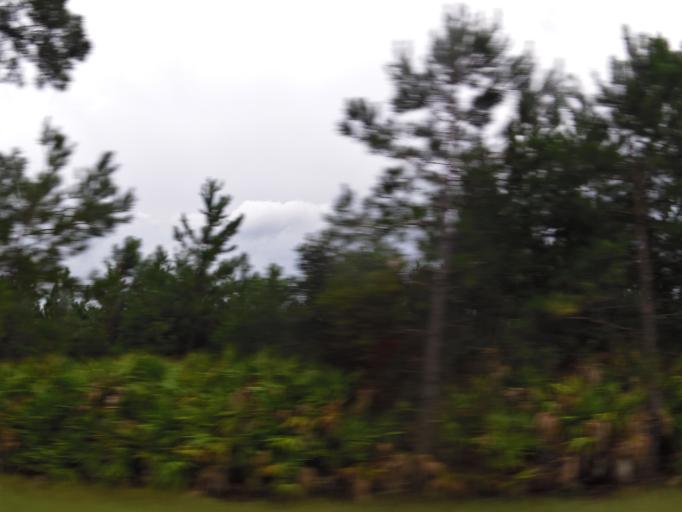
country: US
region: Georgia
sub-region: Wayne County
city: Jesup
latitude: 31.5100
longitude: -81.7660
